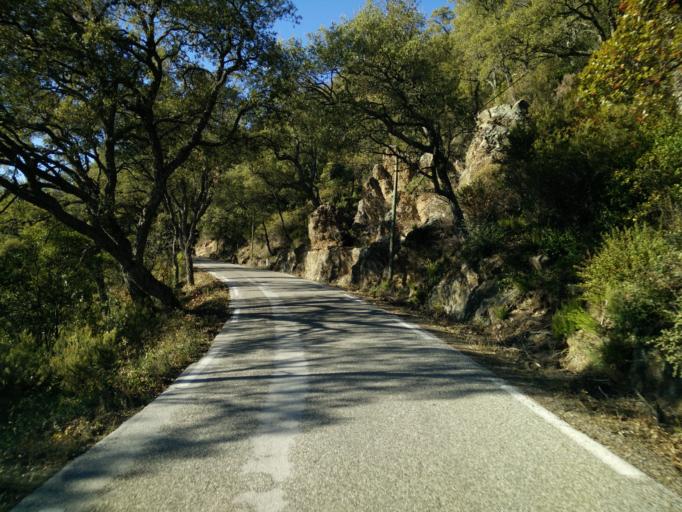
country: FR
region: Provence-Alpes-Cote d'Azur
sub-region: Departement du Var
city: La Garde-Freinet
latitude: 43.2573
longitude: 6.4317
